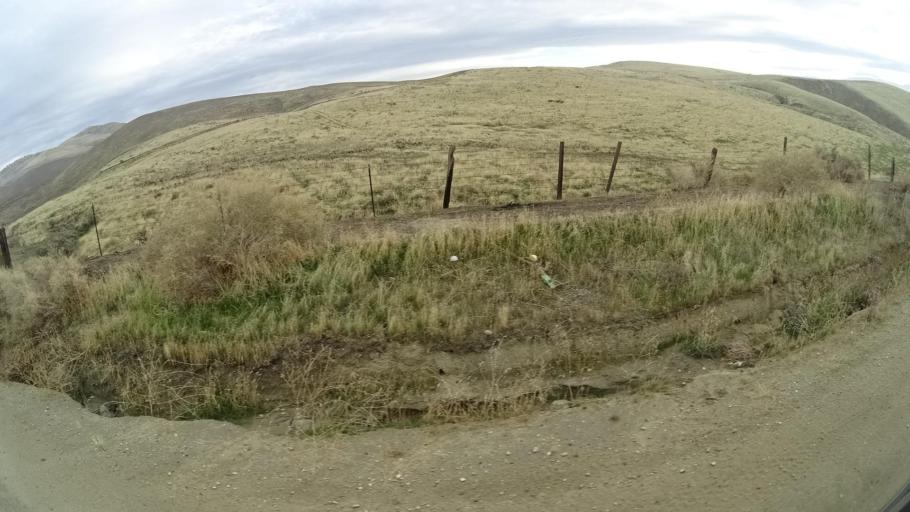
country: US
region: California
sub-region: Kern County
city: Arvin
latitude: 35.1424
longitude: -118.7966
